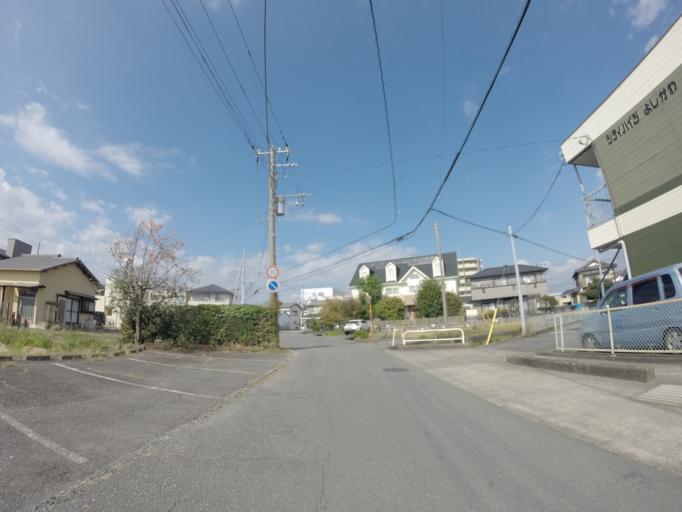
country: JP
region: Shizuoka
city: Fuji
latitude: 35.1403
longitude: 138.6602
